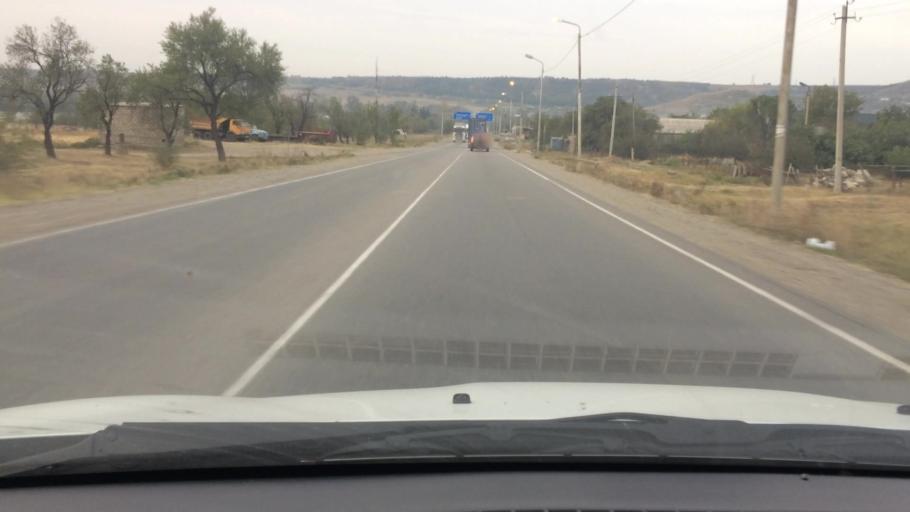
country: GE
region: T'bilisi
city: Tbilisi
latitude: 41.6166
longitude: 44.7922
